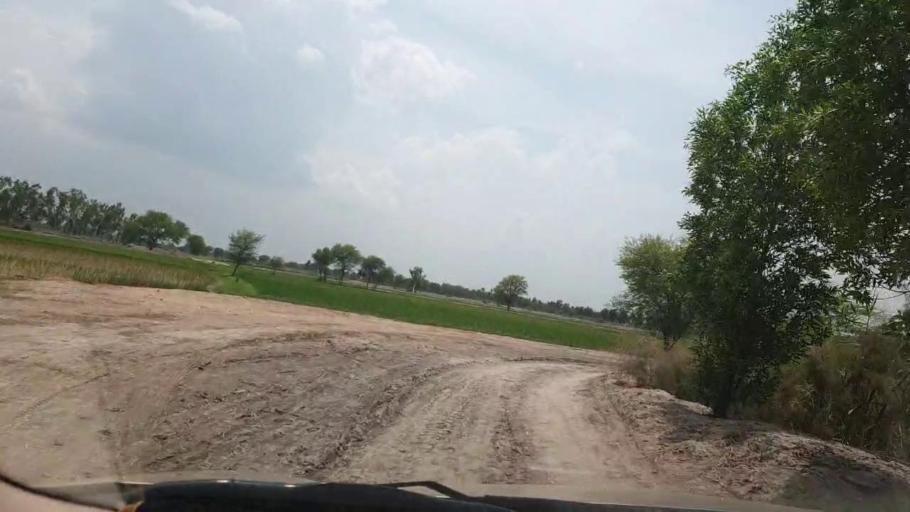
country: PK
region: Sindh
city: Larkana
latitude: 27.6148
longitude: 68.1542
